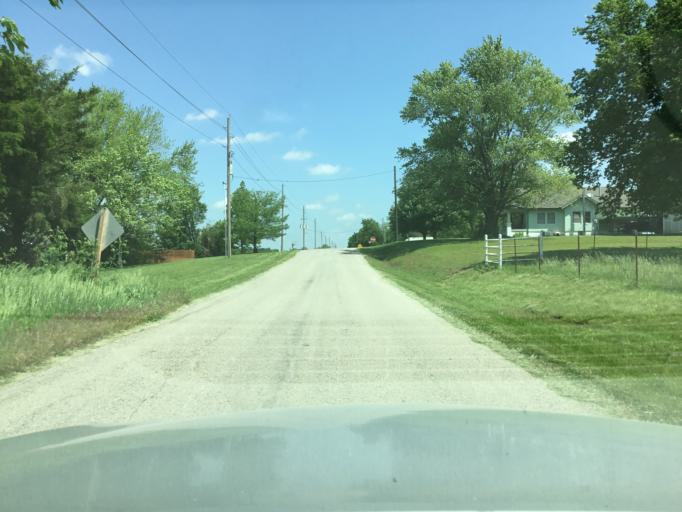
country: US
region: Kansas
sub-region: Labette County
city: Parsons
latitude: 37.3543
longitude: -95.2495
